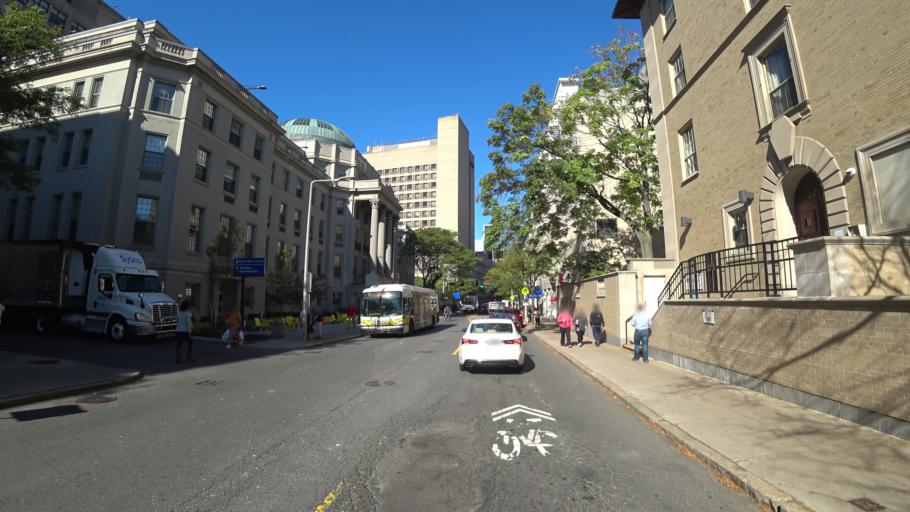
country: US
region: Massachusetts
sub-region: Norfolk County
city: Brookline
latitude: 42.3374
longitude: -71.1042
